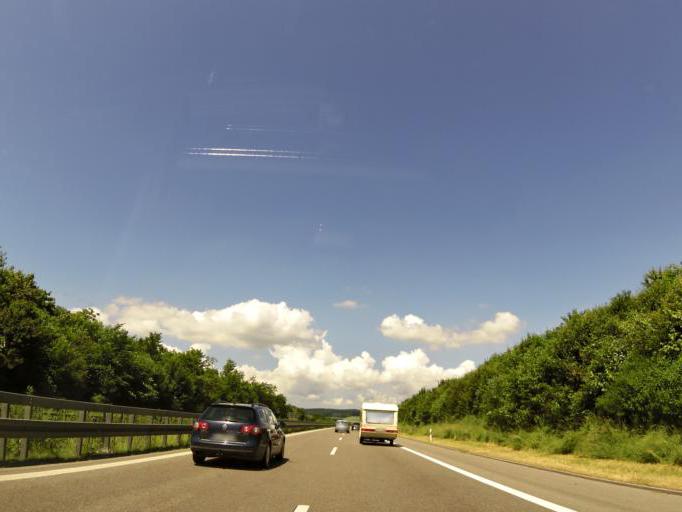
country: DE
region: Baden-Wuerttemberg
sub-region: Tuebingen Region
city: Langenau
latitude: 48.4842
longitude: 10.0984
